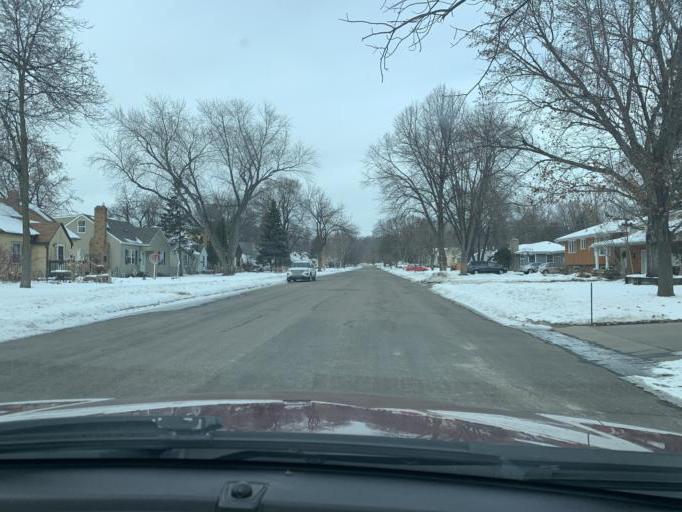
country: US
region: Minnesota
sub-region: Washington County
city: Saint Paul Park
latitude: 44.8429
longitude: -92.9870
